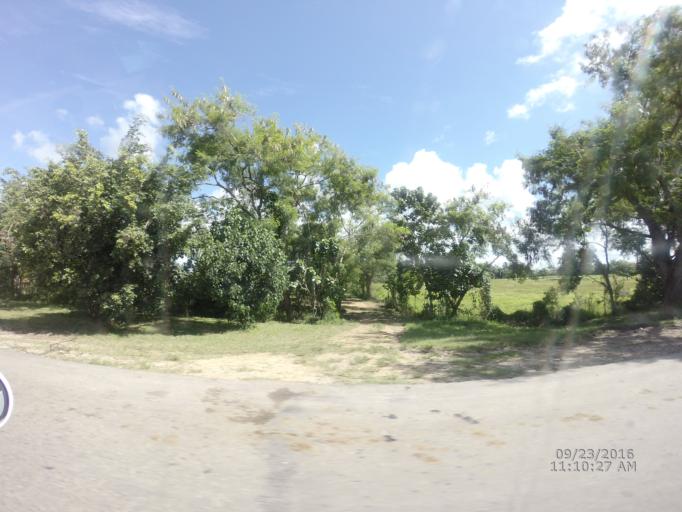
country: CU
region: La Habana
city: Arroyo Naranjo
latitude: 23.0205
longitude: -82.2563
